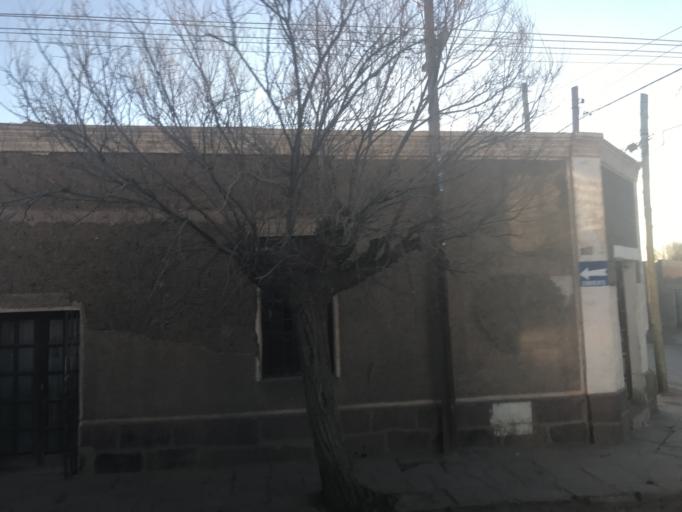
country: AR
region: Jujuy
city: Abra Pampa
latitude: -22.7201
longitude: -65.6972
